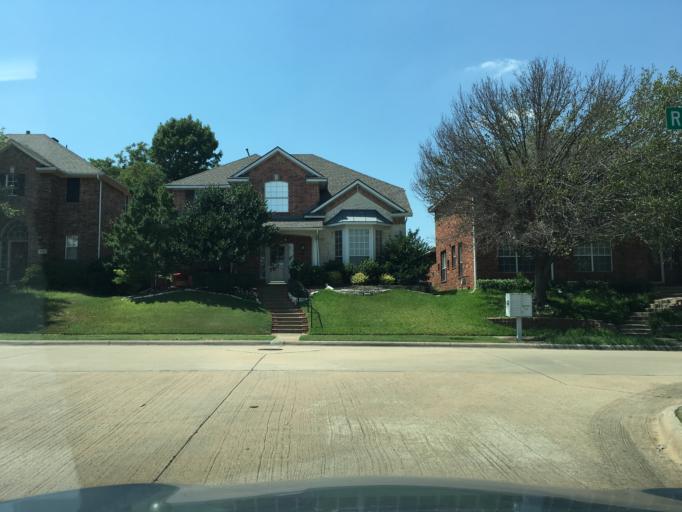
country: US
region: Texas
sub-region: Dallas County
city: Garland
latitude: 32.9651
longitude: -96.6662
